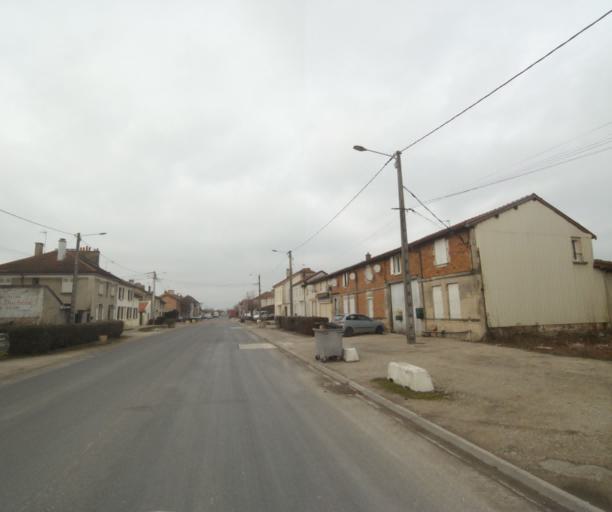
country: FR
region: Champagne-Ardenne
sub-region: Departement de la Haute-Marne
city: Villiers-en-Lieu
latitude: 48.6550
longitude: 4.8251
